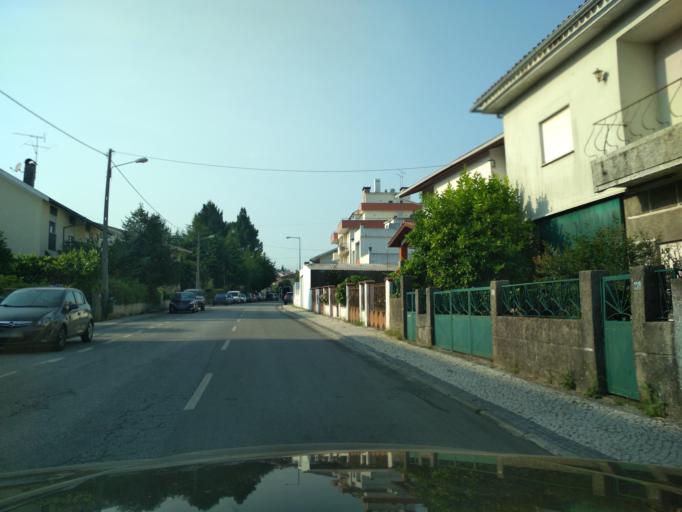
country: PT
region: Viseu
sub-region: Viseu
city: Abraveses
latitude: 40.6742
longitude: -7.9154
